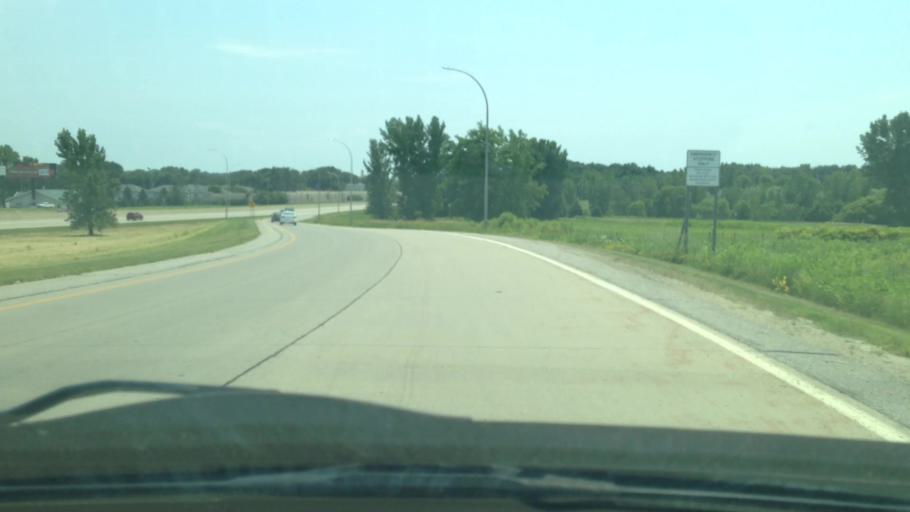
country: US
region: Minnesota
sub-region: Olmsted County
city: Rochester
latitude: 44.0611
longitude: -92.4991
